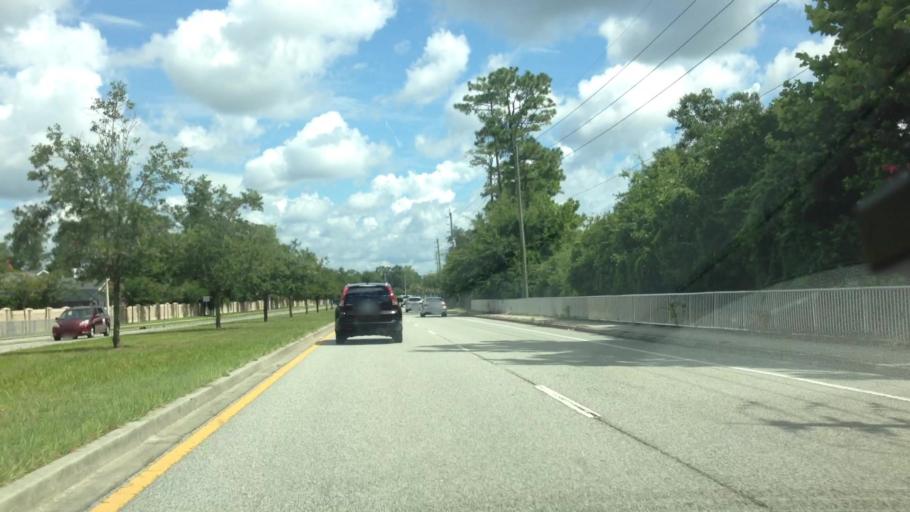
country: US
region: Florida
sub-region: Duval County
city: Neptune Beach
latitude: 30.3068
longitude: -81.4591
